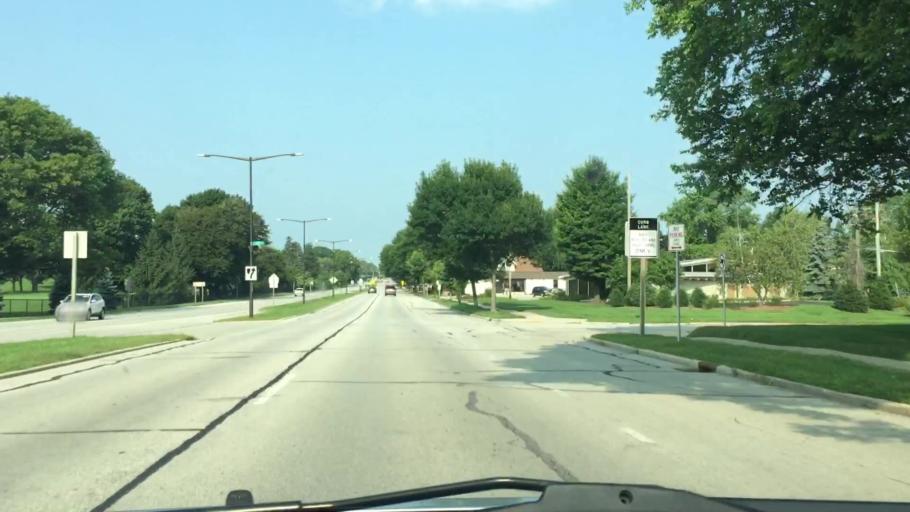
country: US
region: Wisconsin
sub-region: Waukesha County
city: Elm Grove
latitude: 43.0165
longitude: -88.0580
